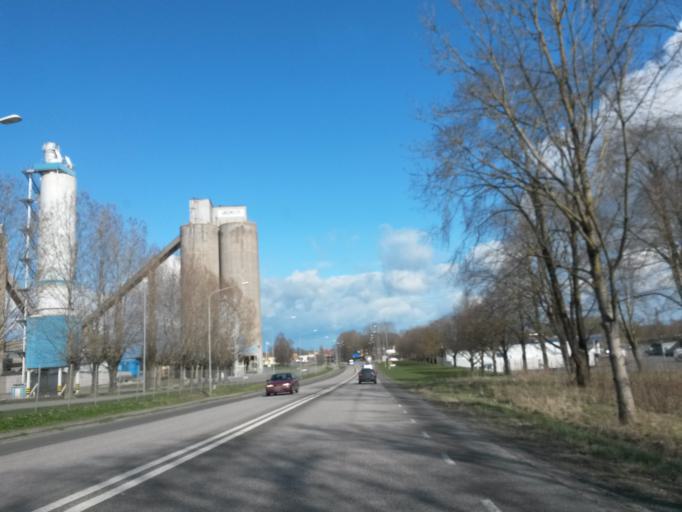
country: SE
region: Vaestra Goetaland
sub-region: Skovde Kommun
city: Skoevde
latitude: 58.3822
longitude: 13.8247
